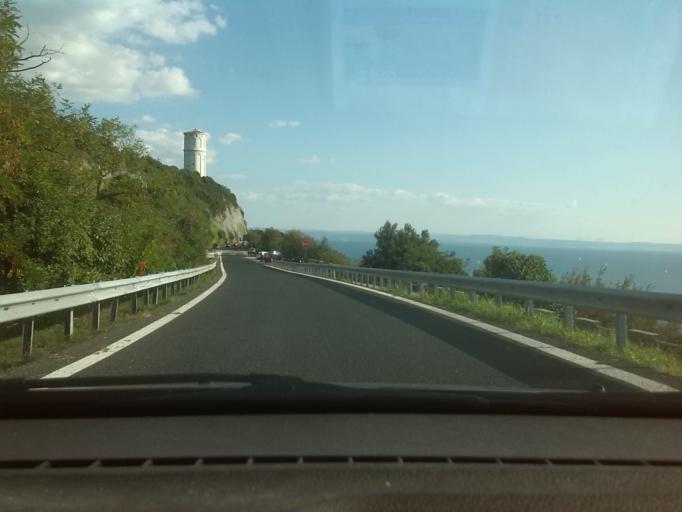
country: IT
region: Friuli Venezia Giulia
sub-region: Provincia di Trieste
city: Sistiana-Visogliano
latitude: 45.7612
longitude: 13.6400
